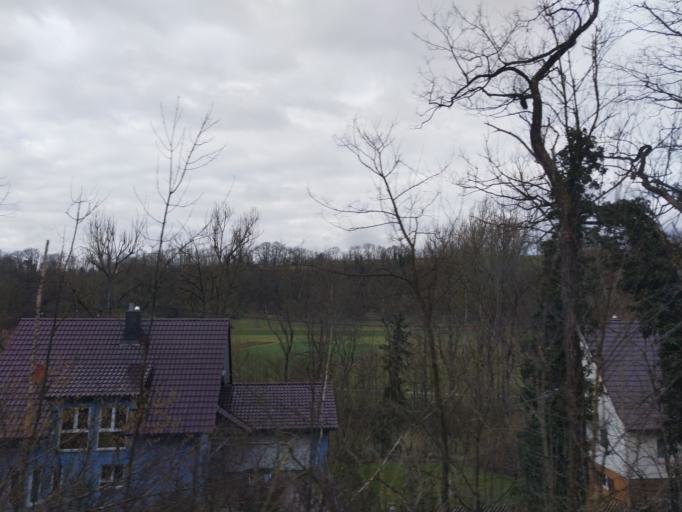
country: DE
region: Baden-Wuerttemberg
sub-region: Regierungsbezirk Stuttgart
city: Burgstetten
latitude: 48.9306
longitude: 9.3732
